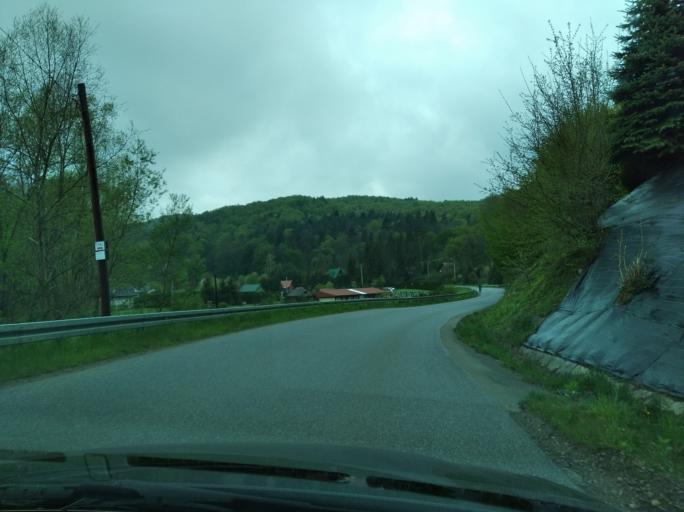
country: PL
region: Subcarpathian Voivodeship
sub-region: Powiat sanocki
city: Sanok
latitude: 49.6042
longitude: 22.2098
